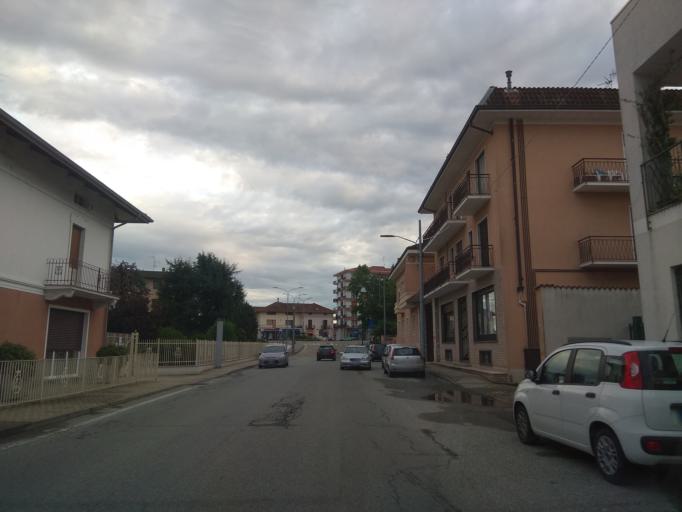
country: IT
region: Piedmont
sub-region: Provincia di Biella
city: Cerreto Castello
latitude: 45.5664
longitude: 8.1673
